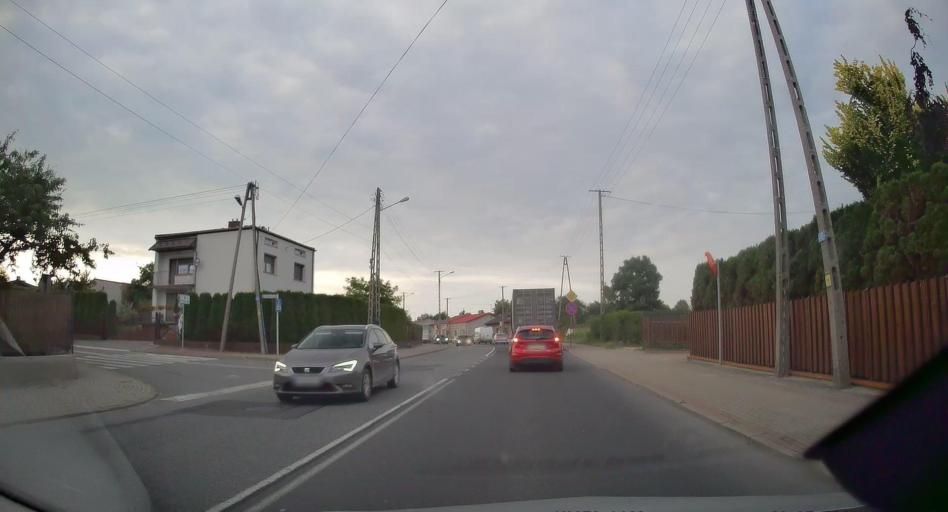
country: PL
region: Lodz Voivodeship
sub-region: Powiat radomszczanski
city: Kamiensk
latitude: 51.2001
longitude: 19.4998
